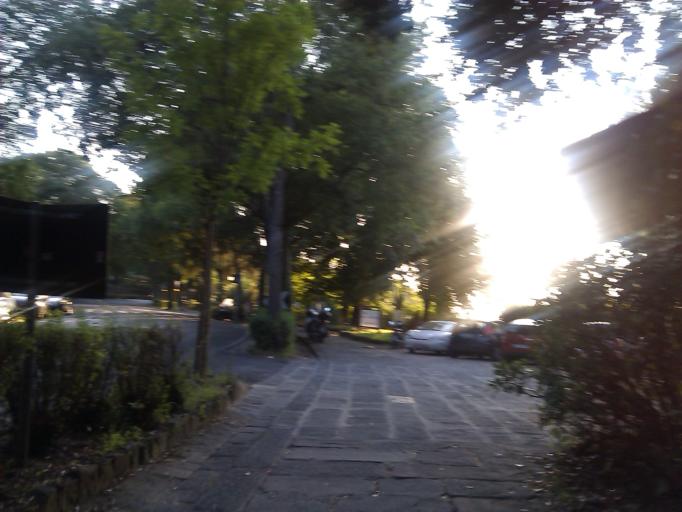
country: IT
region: Tuscany
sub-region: Province of Florence
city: Florence
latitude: 43.7613
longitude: 11.2696
